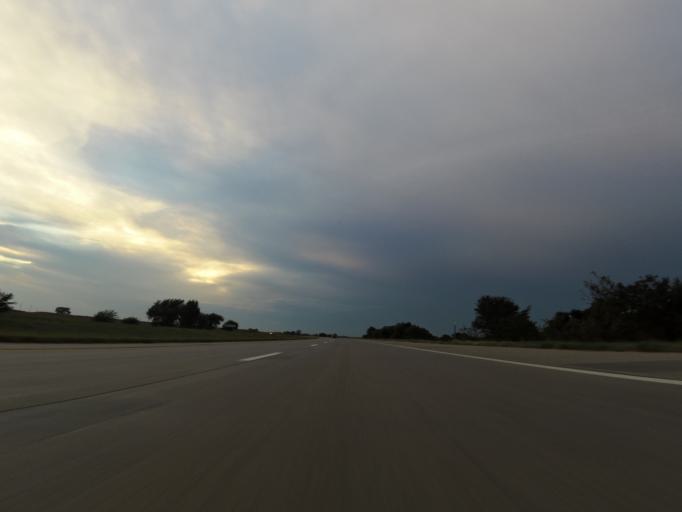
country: US
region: Kansas
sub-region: Sedgwick County
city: Colwich
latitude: 37.8399
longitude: -97.5732
